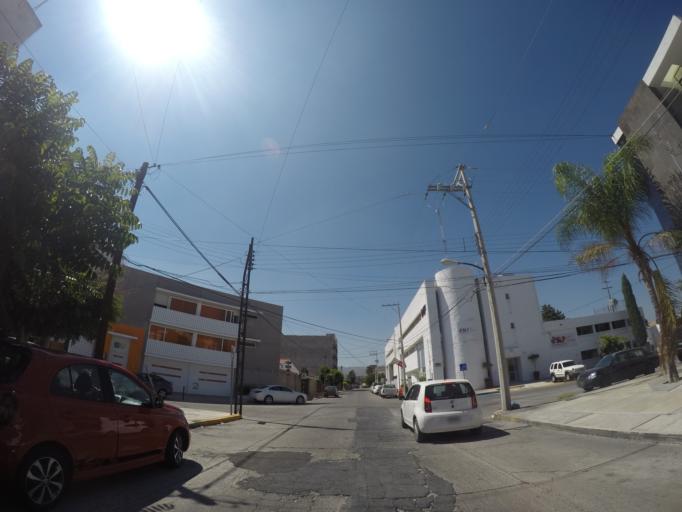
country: MX
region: San Luis Potosi
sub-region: San Luis Potosi
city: San Luis Potosi
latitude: 22.1446
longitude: -101.0097
